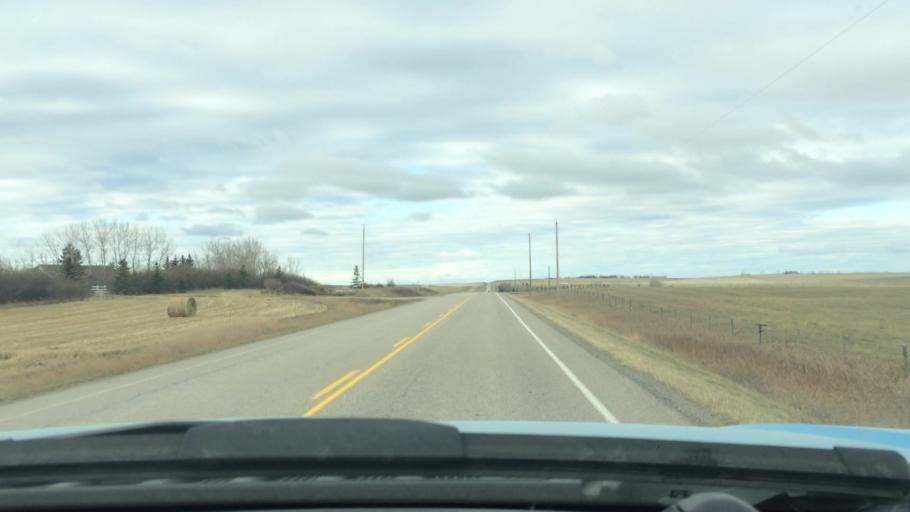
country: CA
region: Alberta
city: Airdrie
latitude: 51.2125
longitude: -114.0758
